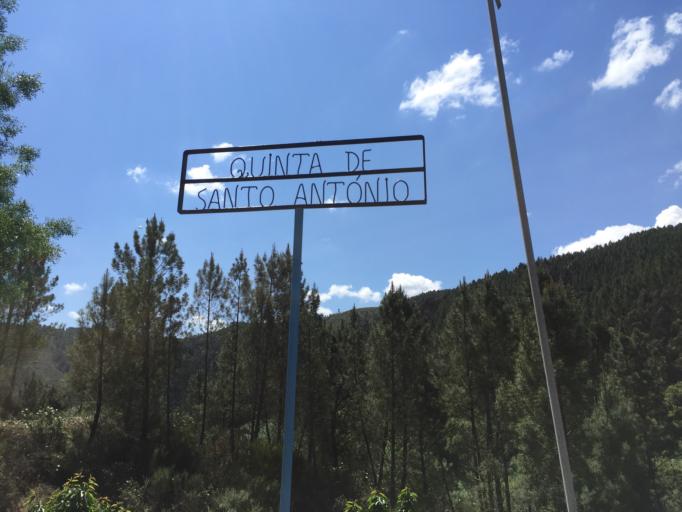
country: PT
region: Coimbra
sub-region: Pampilhosa da Serra
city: Pampilhosa da Serra
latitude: 40.0707
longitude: -7.7813
